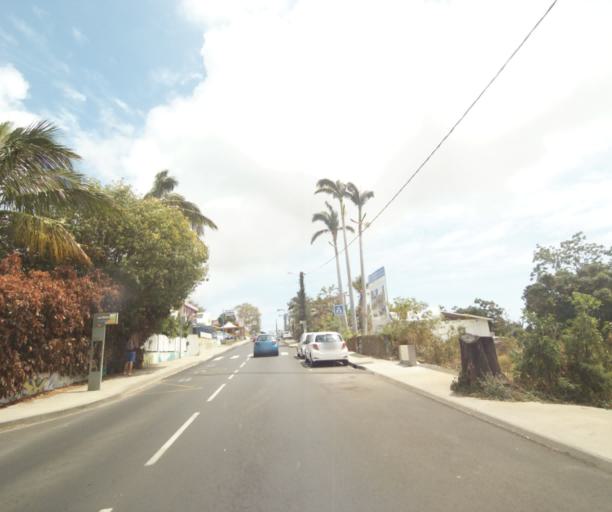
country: RE
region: Reunion
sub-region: Reunion
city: Saint-Paul
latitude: -21.0465
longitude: 55.2678
